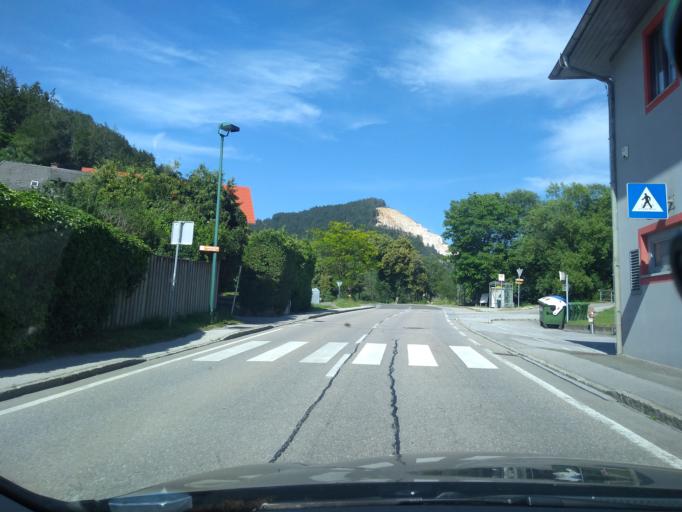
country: AT
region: Styria
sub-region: Politischer Bezirk Graz-Umgebung
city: Deutschfeistritz
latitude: 47.1701
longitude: 15.3367
